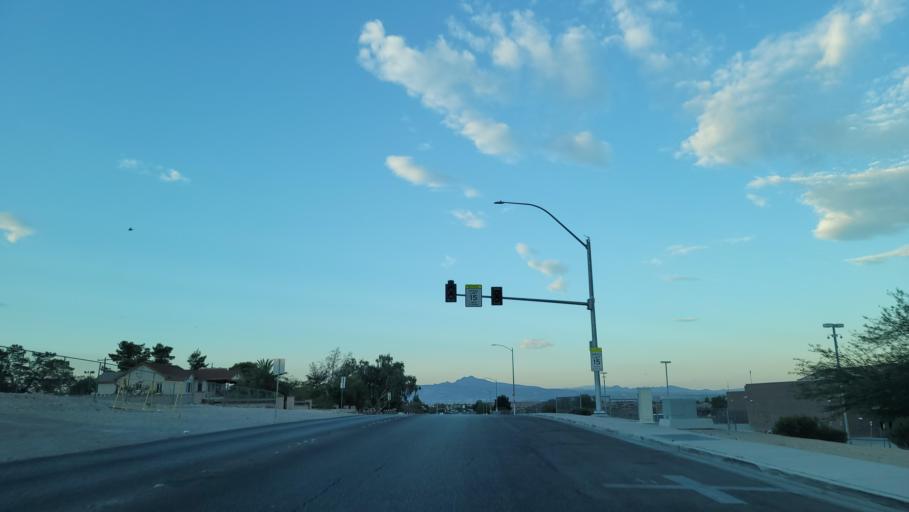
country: US
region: Nevada
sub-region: Clark County
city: Sunrise Manor
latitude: 36.1666
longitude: -115.0352
